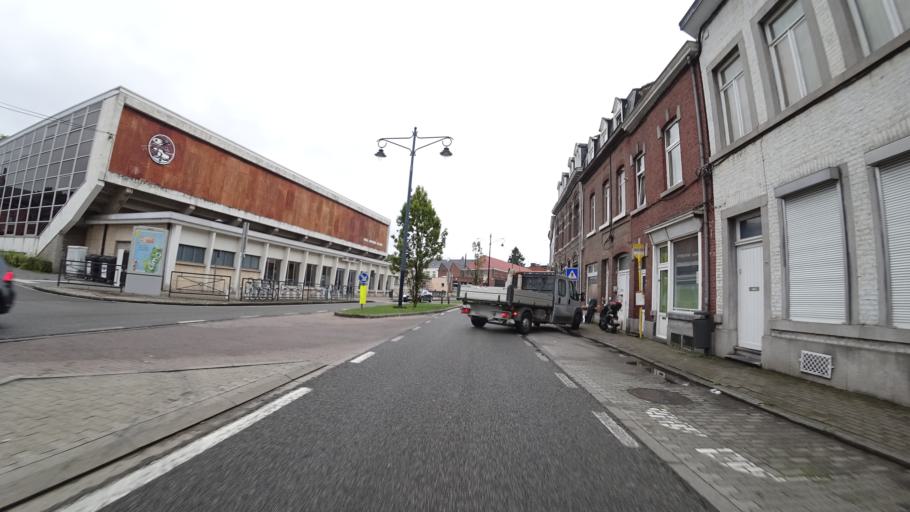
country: BE
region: Wallonia
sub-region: Province de Namur
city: Namur
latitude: 50.4755
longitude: 4.8464
